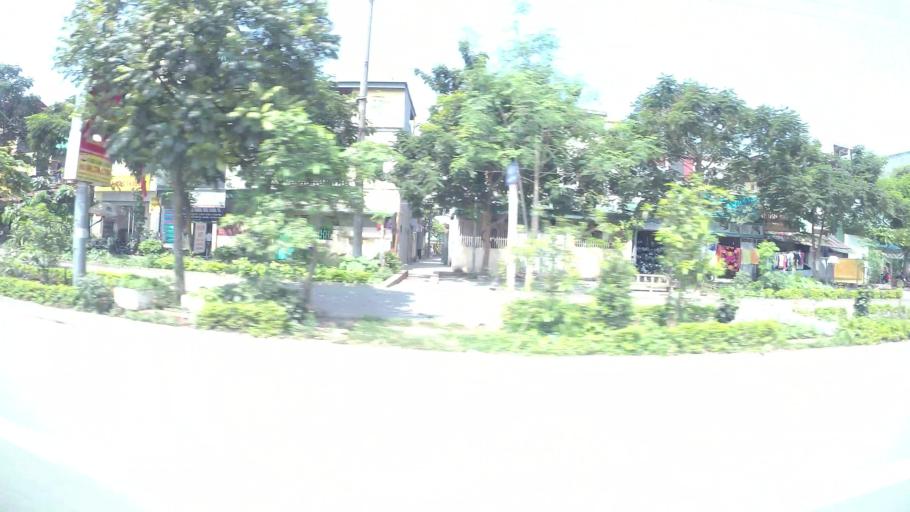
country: VN
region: Ha Noi
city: Hoan Kiem
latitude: 21.0652
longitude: 105.8809
